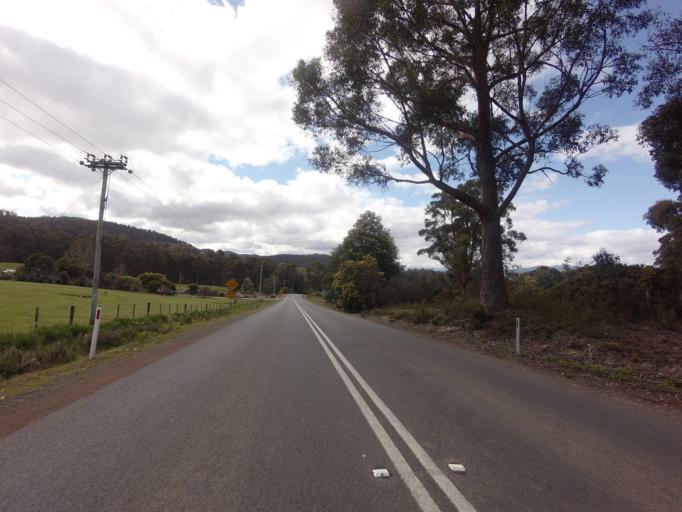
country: AU
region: Tasmania
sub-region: Huon Valley
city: Geeveston
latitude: -43.1966
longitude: 146.9569
